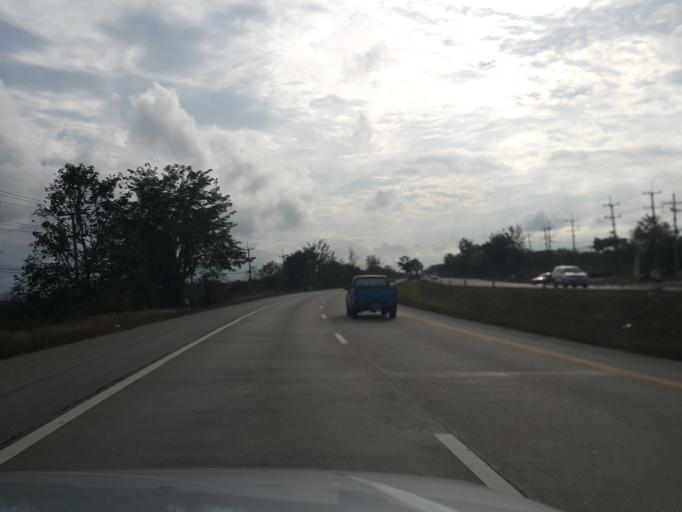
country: TH
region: Lampang
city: Ko Kha
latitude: 18.2142
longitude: 99.4218
